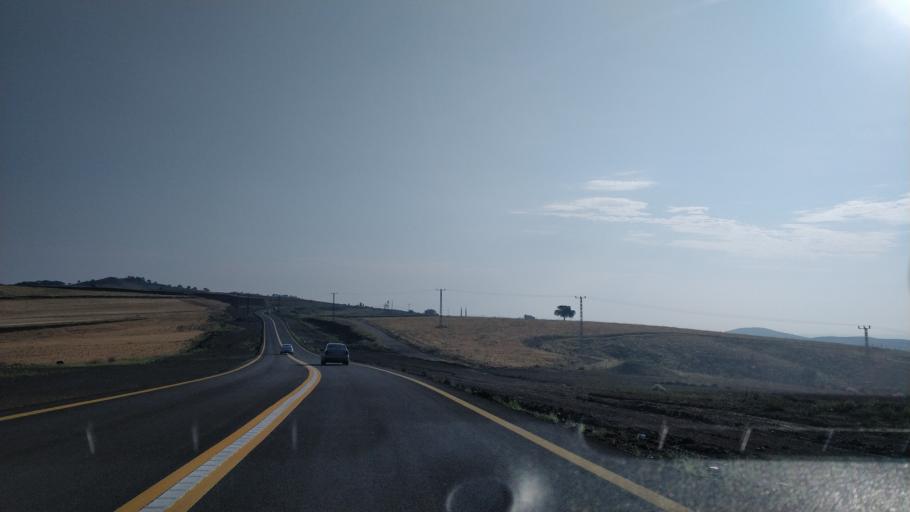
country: TR
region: Ankara
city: Etimesgut
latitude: 39.8580
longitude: 32.5699
